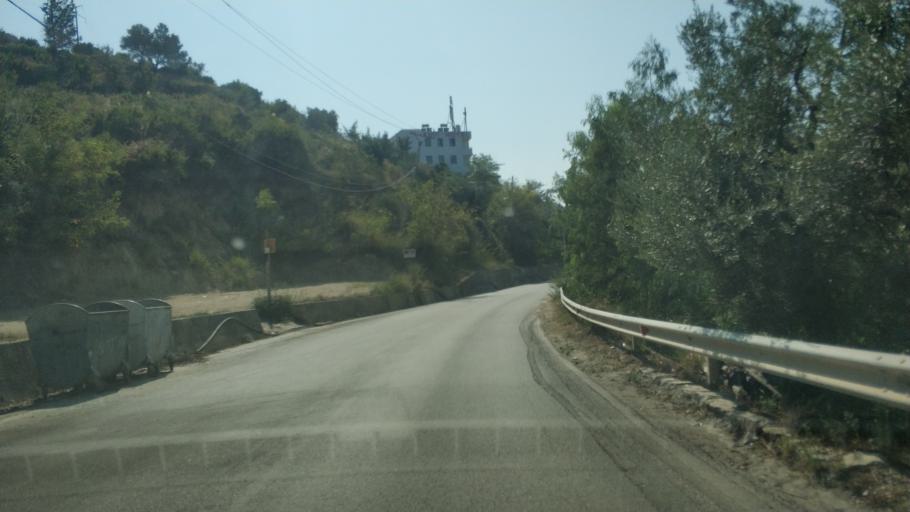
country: AL
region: Vlore
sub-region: Rrethi i Vlores
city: Orikum
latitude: 40.3898
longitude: 19.4818
